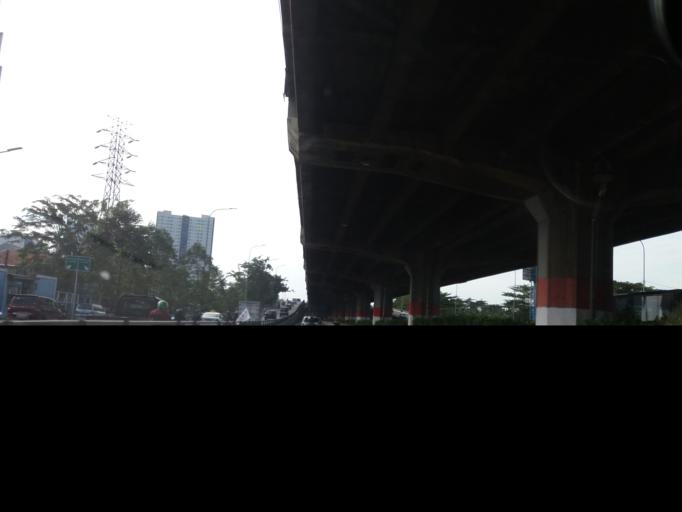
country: ID
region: Jakarta Raya
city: Jakarta
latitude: -6.1951
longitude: 106.8743
